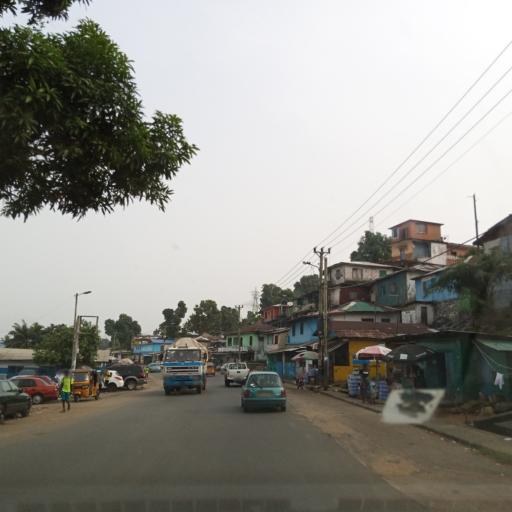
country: LR
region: Montserrado
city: Monrovia
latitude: 6.3044
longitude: -10.7949
